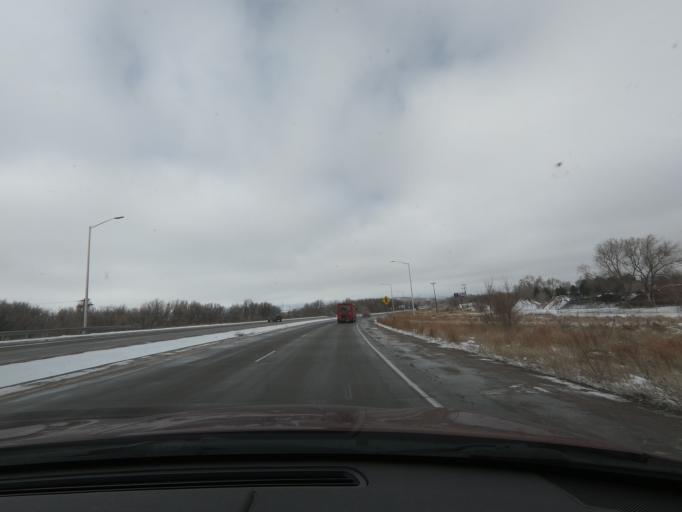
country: US
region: Colorado
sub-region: El Paso County
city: Security-Widefield
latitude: 38.7232
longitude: -104.7226
